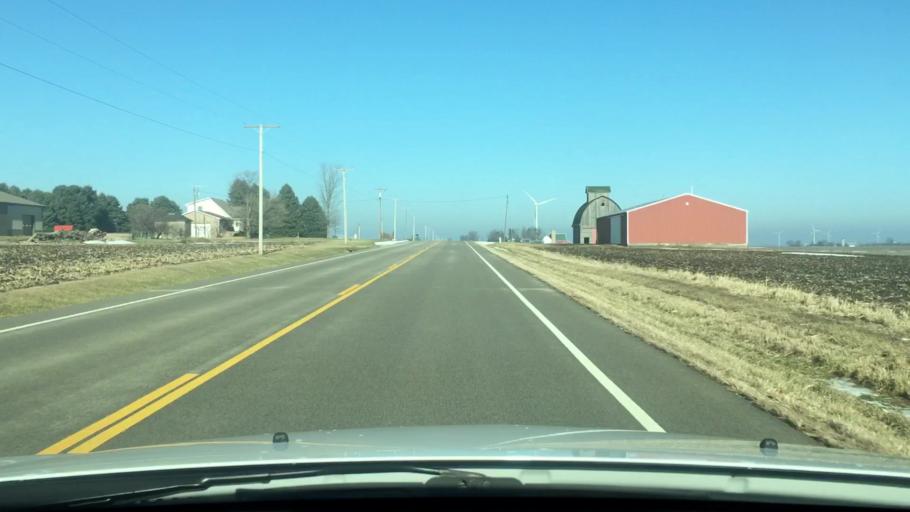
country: US
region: Illinois
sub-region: DeKalb County
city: Malta
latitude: 41.8286
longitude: -88.8864
